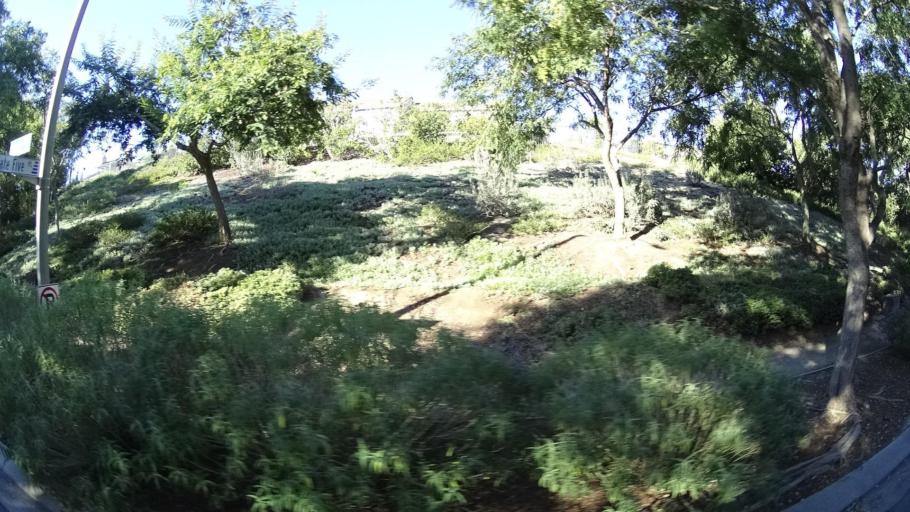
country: US
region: California
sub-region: San Diego County
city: La Presa
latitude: 32.6529
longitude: -116.9407
